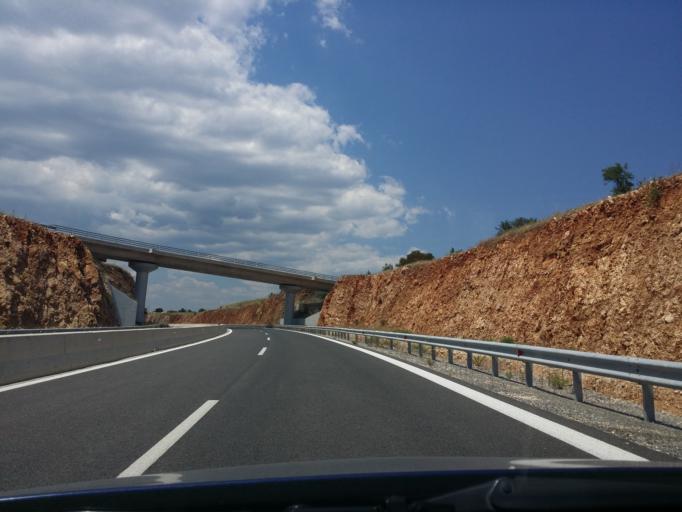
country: GR
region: Peloponnese
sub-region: Nomos Arkadias
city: Megalopoli
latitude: 37.2868
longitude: 22.2144
